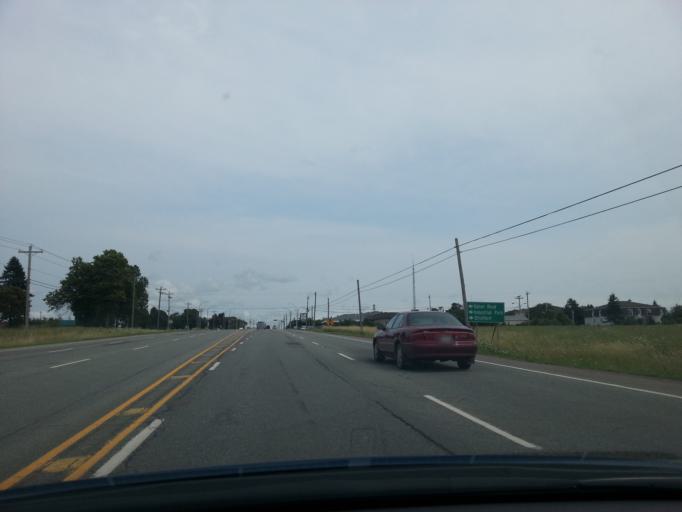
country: CA
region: Prince Edward Island
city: Charlottetown
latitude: 46.2603
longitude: -63.1730
